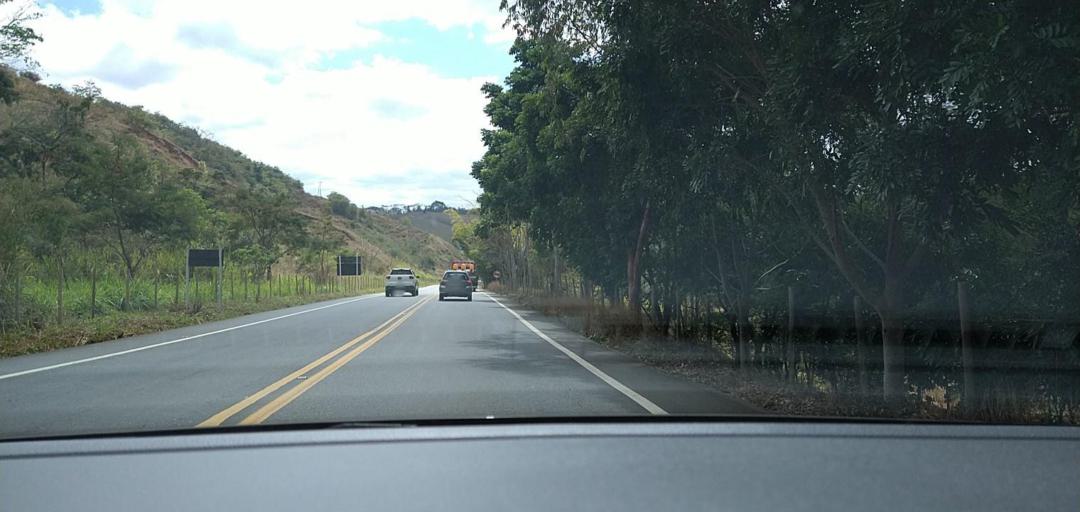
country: BR
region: Minas Gerais
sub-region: Ponte Nova
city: Ponte Nova
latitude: -20.5068
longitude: -42.8793
